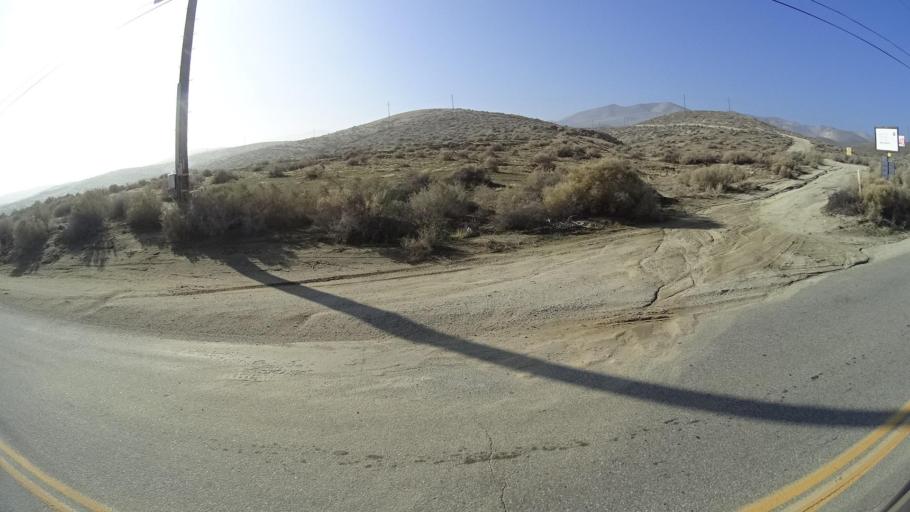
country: US
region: California
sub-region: Kern County
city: Taft Heights
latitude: 35.1921
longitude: -119.5755
